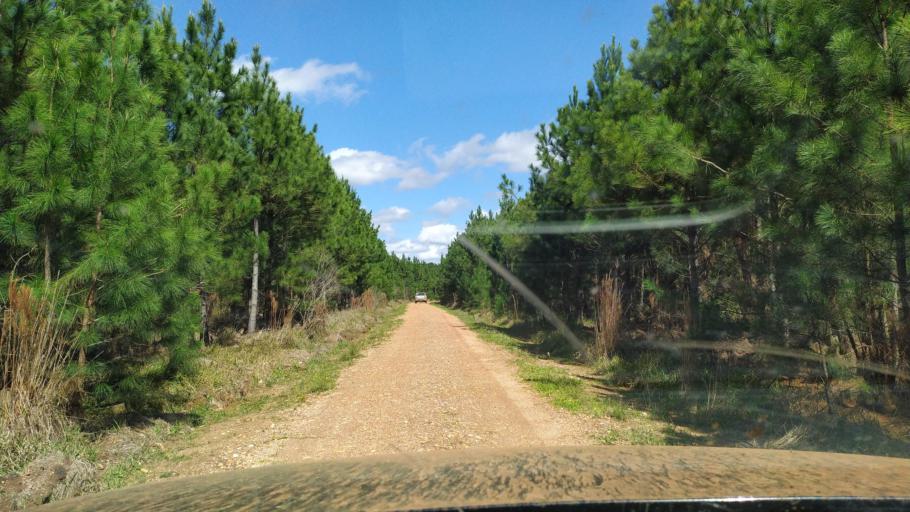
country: AR
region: Corrientes
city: Santo Tome
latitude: -28.4612
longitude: -55.9874
